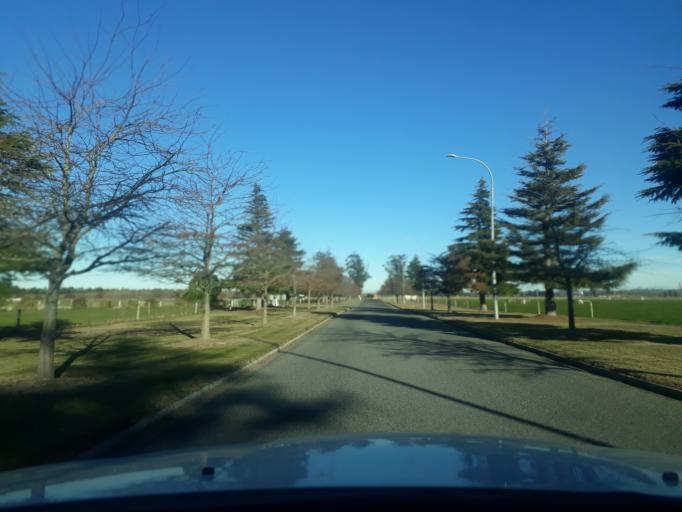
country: NZ
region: Canterbury
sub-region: Timaru District
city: Timaru
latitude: -44.3069
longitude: 171.2257
